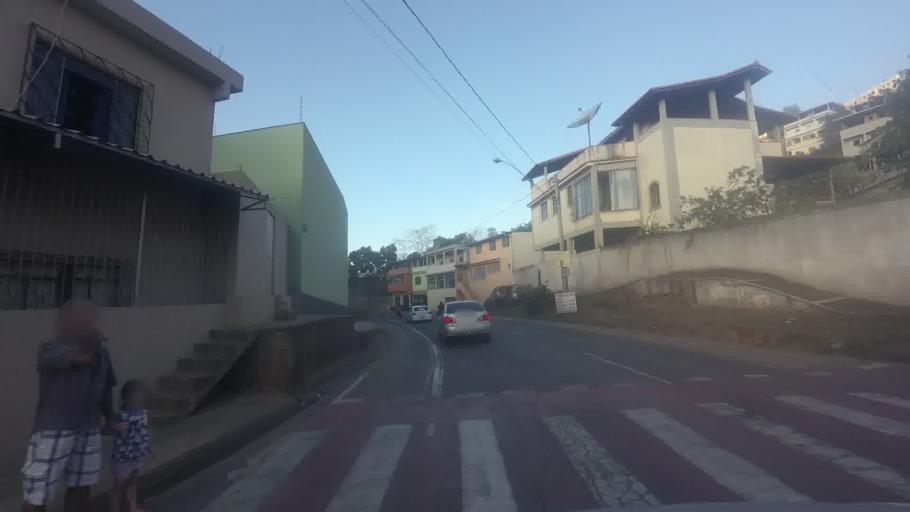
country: BR
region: Espirito Santo
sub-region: Cachoeiro De Itapemirim
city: Cachoeiro de Itapemirim
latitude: -20.8504
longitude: -41.1425
